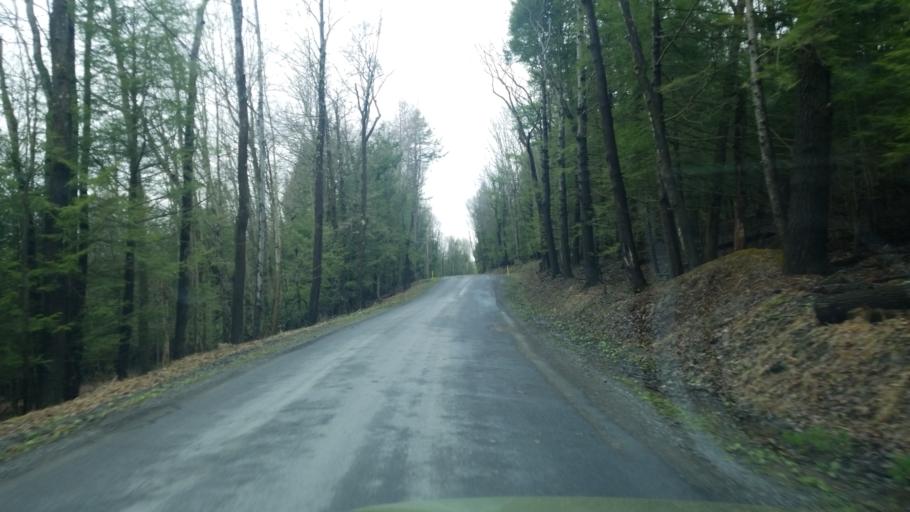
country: US
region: Pennsylvania
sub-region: Clearfield County
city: Shiloh
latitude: 41.1167
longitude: -78.3414
